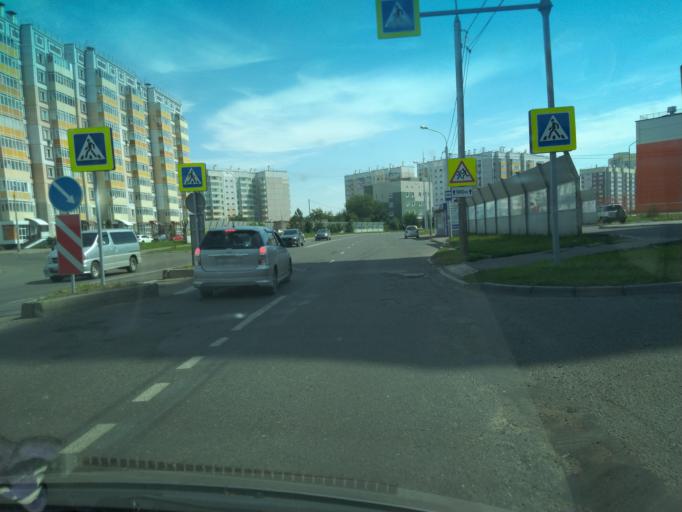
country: RU
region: Krasnoyarskiy
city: Solnechnyy
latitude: 56.0540
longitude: 92.9208
